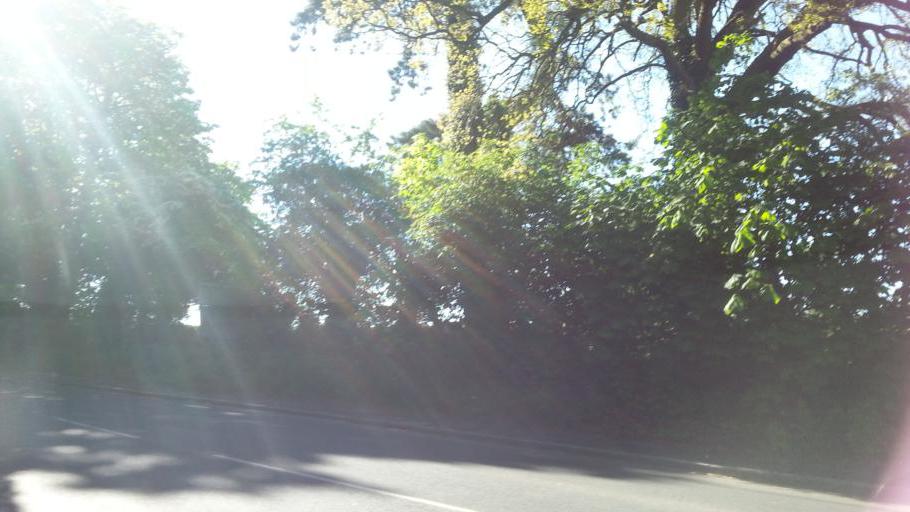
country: GB
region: England
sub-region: Somerset
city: Milborne Port
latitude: 50.9650
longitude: -2.4679
